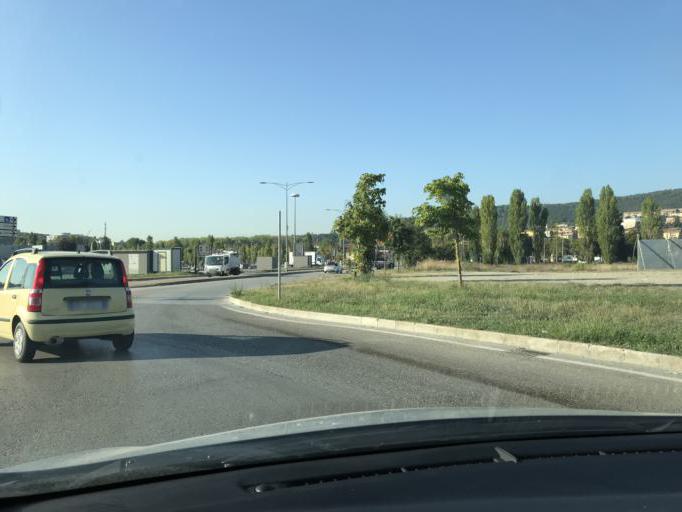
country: IT
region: Umbria
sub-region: Provincia di Perugia
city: Perugia
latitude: 43.1112
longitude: 12.3602
